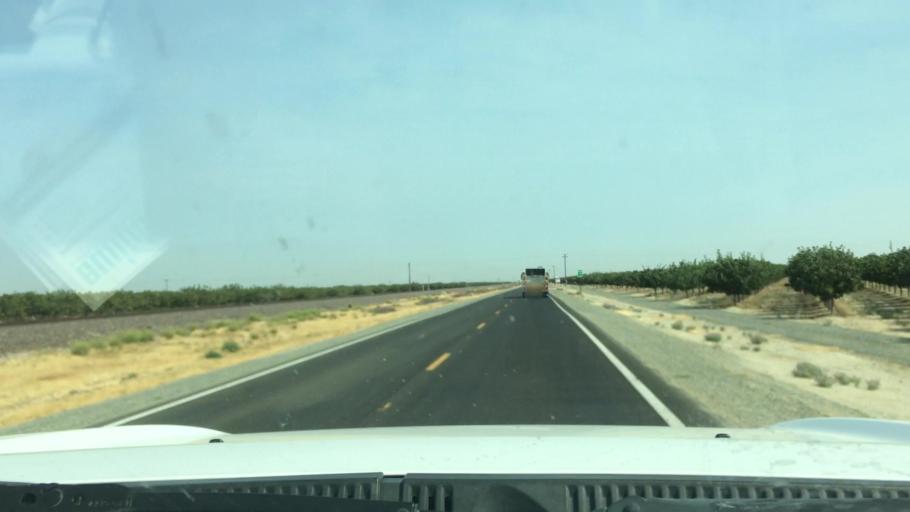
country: US
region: California
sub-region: Tulare County
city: Earlimart
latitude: 35.8163
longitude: -119.3641
